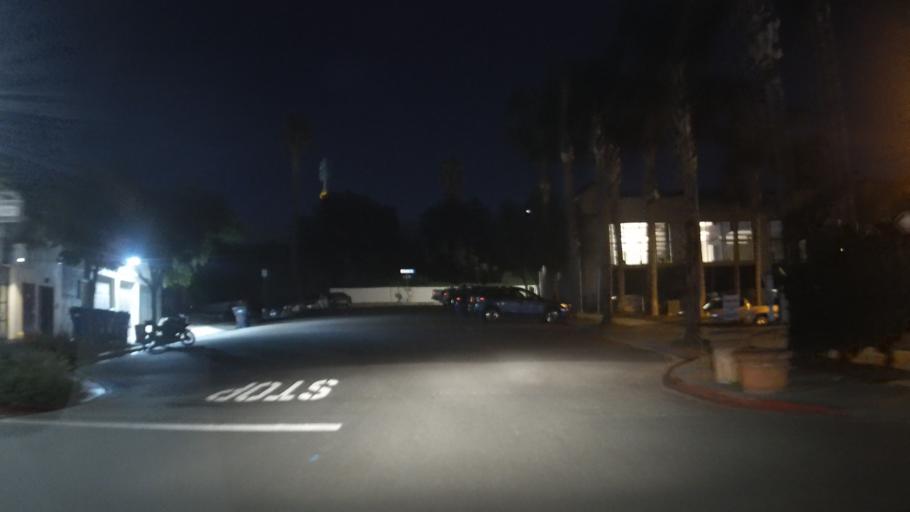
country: US
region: California
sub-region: San Diego County
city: San Diego
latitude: 32.7283
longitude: -117.1703
